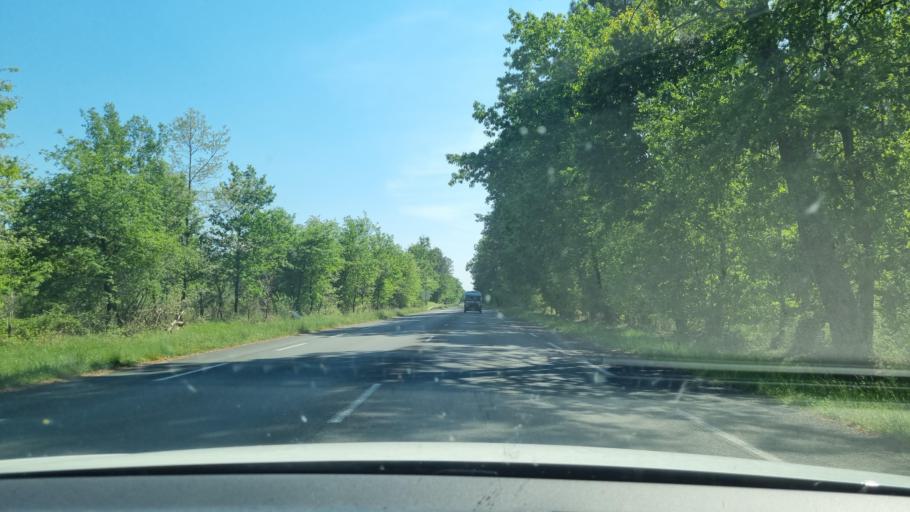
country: FR
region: Aquitaine
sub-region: Departement des Landes
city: Roquefort
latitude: 44.2004
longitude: -0.2702
